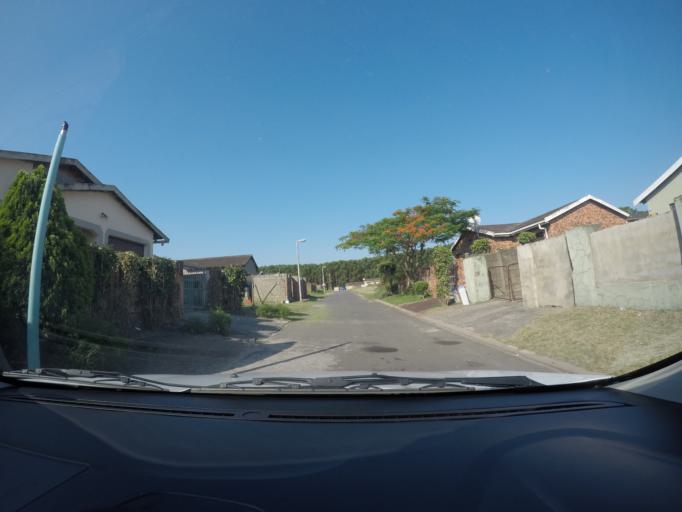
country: ZA
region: KwaZulu-Natal
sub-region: uThungulu District Municipality
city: Richards Bay
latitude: -28.7137
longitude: 32.0408
